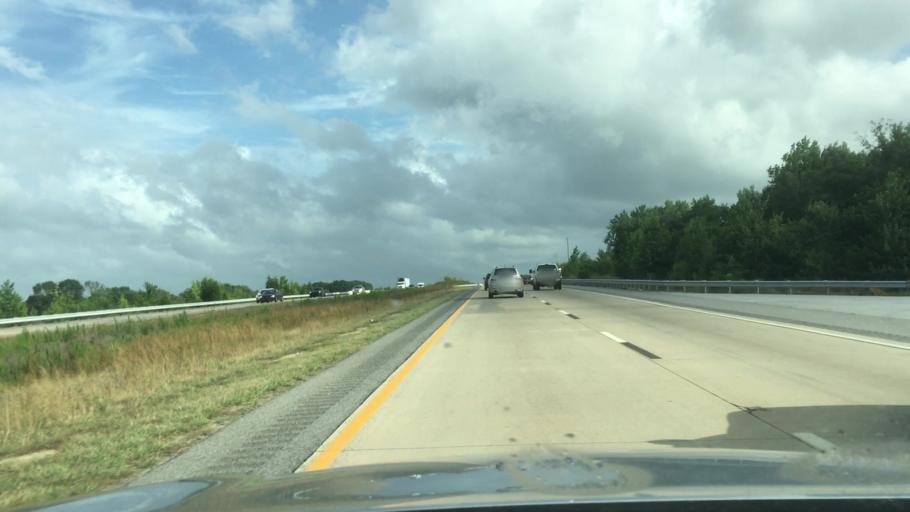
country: US
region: Delaware
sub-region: New Castle County
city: Townsend
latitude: 39.3885
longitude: -75.6658
